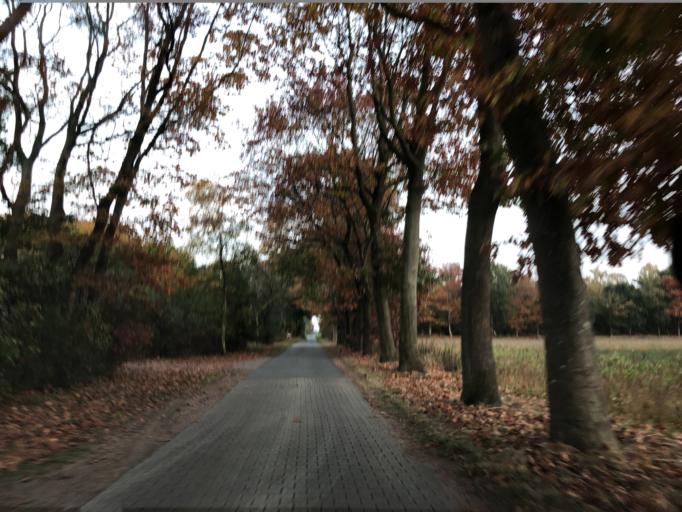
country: DE
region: Lower Saxony
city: Neulehe
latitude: 53.0304
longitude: 7.3750
